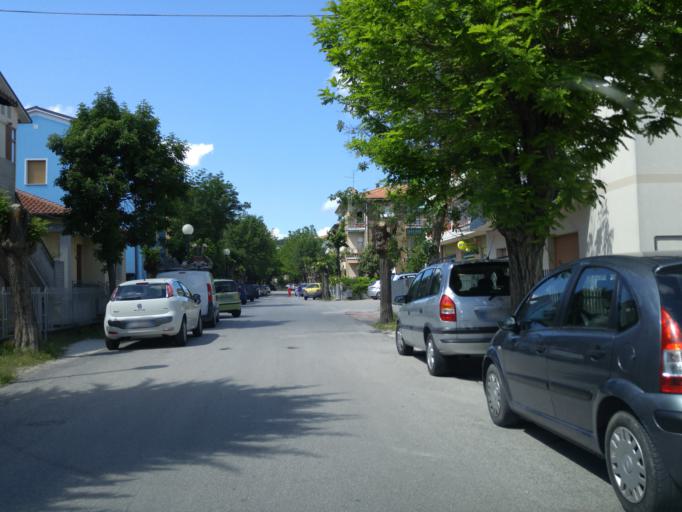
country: IT
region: The Marches
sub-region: Provincia di Pesaro e Urbino
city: Fermignano
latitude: 43.6808
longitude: 12.6464
